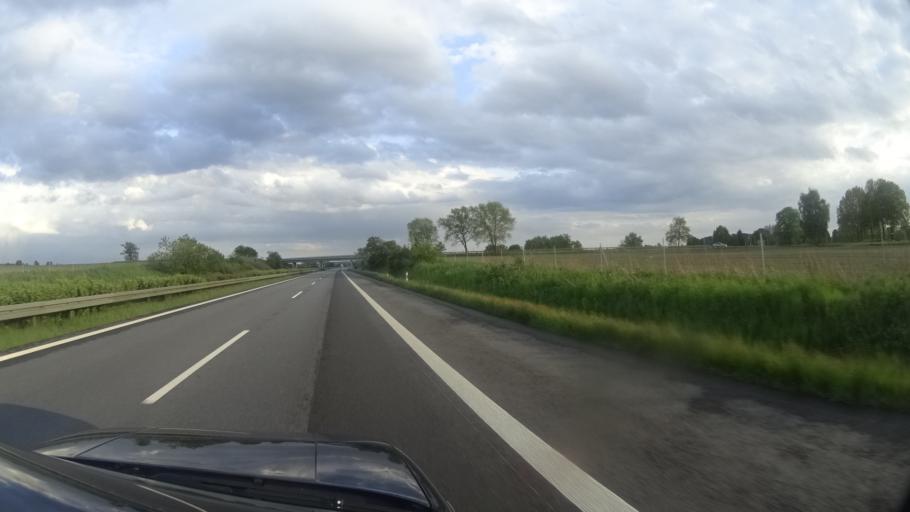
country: DE
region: Brandenburg
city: Wittstock
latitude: 53.2020
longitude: 12.4537
